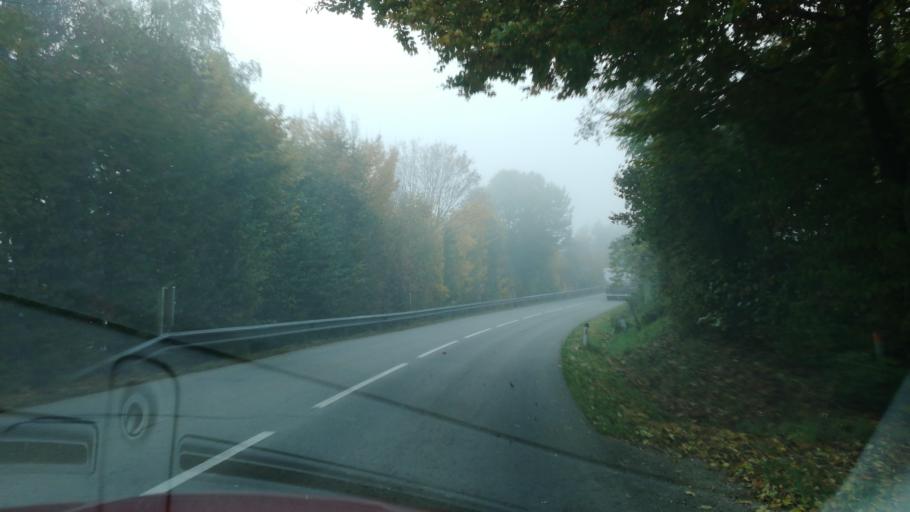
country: AT
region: Upper Austria
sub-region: Politischer Bezirk Grieskirchen
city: Bad Schallerbach
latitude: 48.1807
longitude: 13.9095
